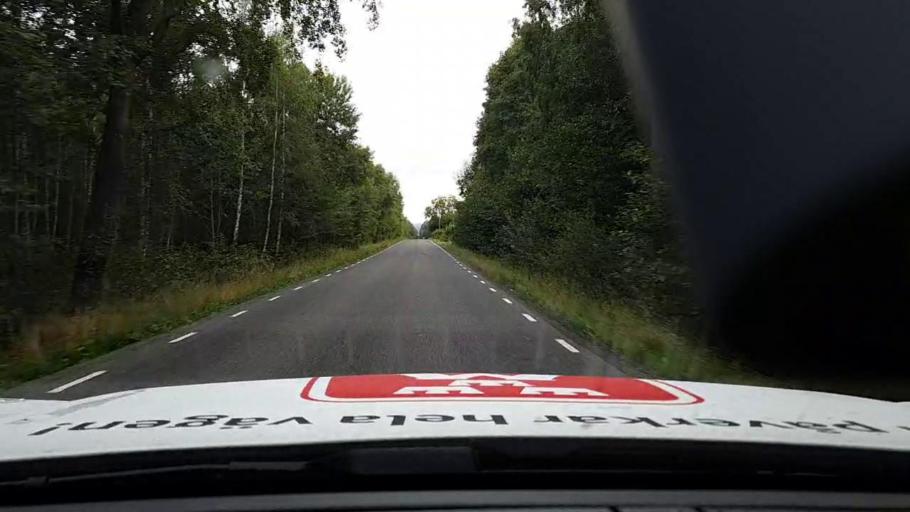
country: SE
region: Skane
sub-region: Hassleholms Kommun
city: Vinslov
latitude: 56.0700
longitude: 13.9016
